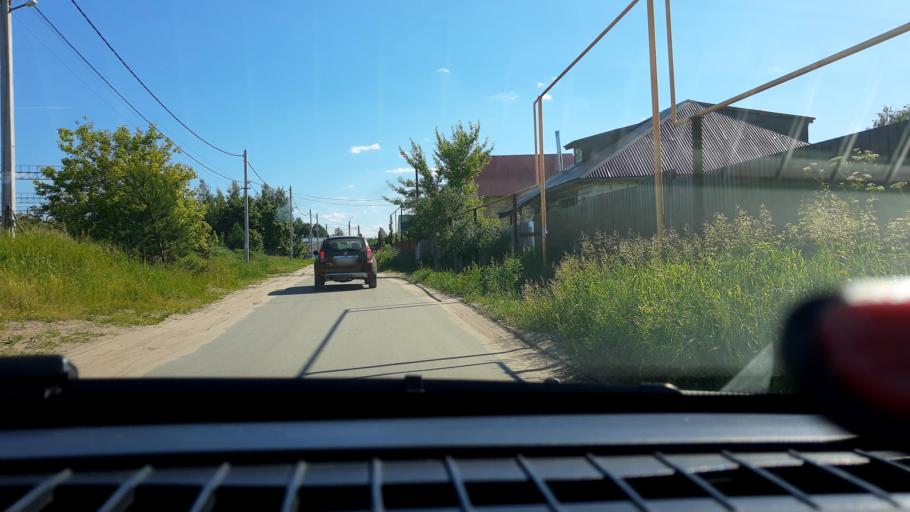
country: RU
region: Nizjnij Novgorod
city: Gidrotorf
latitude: 56.5116
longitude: 43.5356
